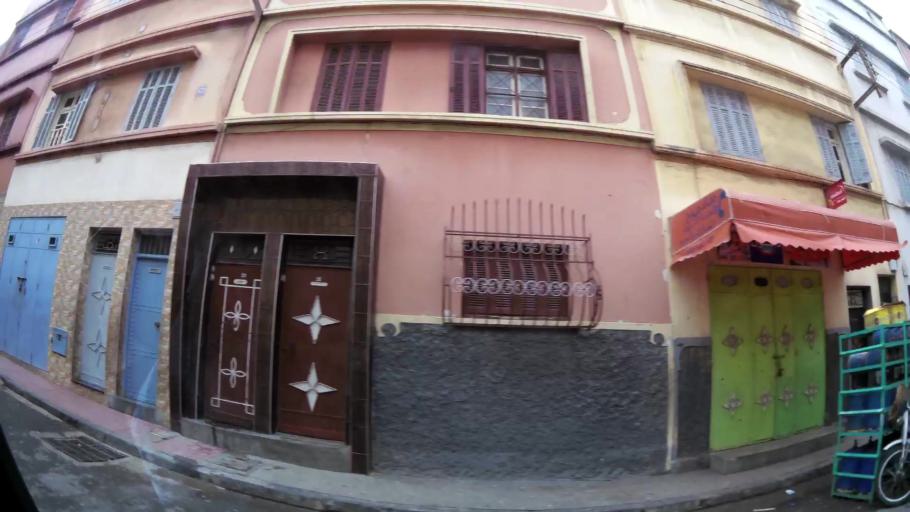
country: MA
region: Grand Casablanca
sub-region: Casablanca
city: Casablanca
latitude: 33.5470
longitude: -7.5698
